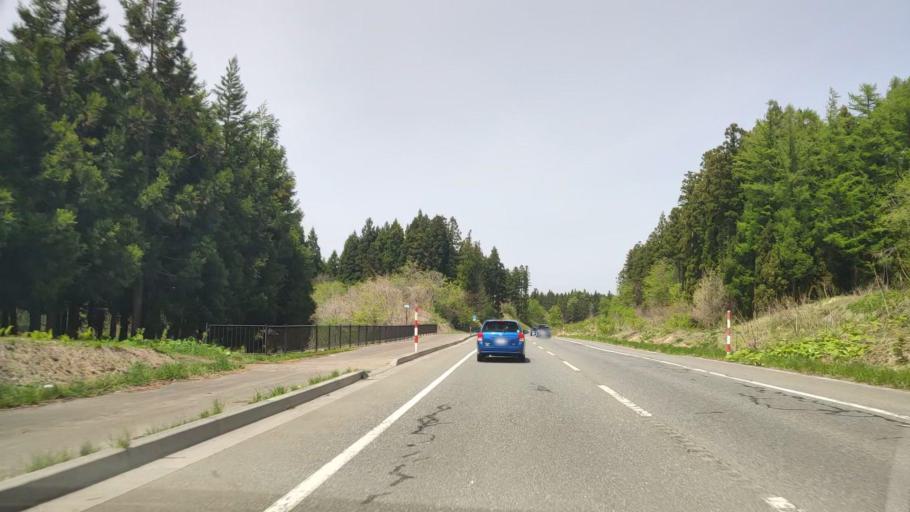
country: JP
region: Aomori
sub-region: Misawa Shi
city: Inuotose
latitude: 40.6866
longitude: 141.1698
